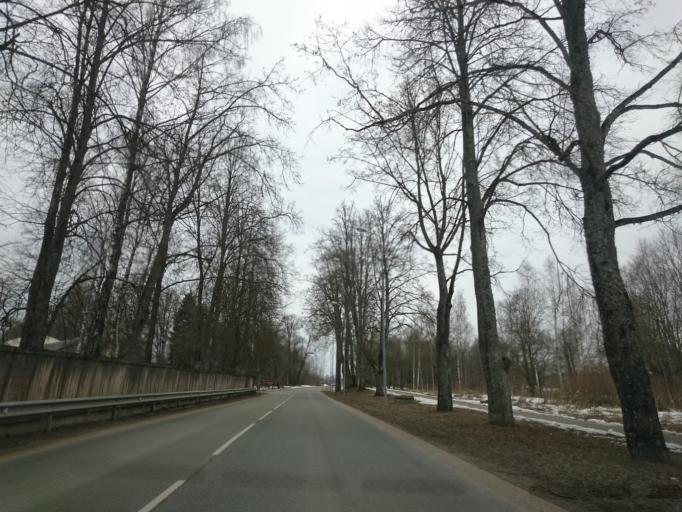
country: LV
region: Cesu Rajons
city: Cesis
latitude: 57.2957
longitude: 25.2618
